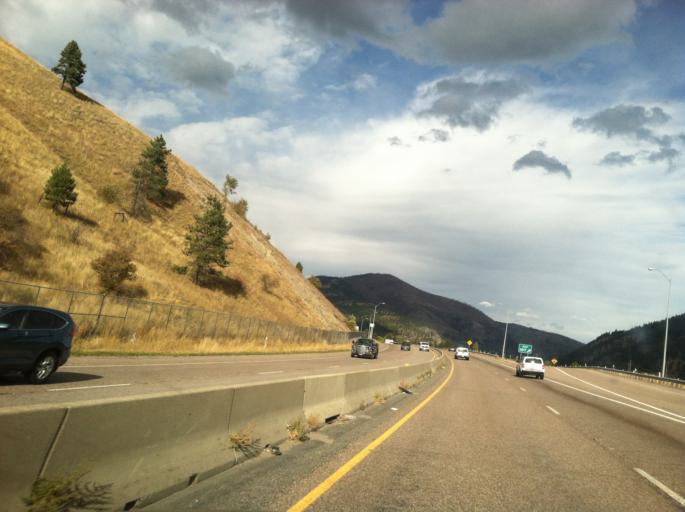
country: US
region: Montana
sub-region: Missoula County
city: East Missoula
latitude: 46.8647
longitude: -113.9563
